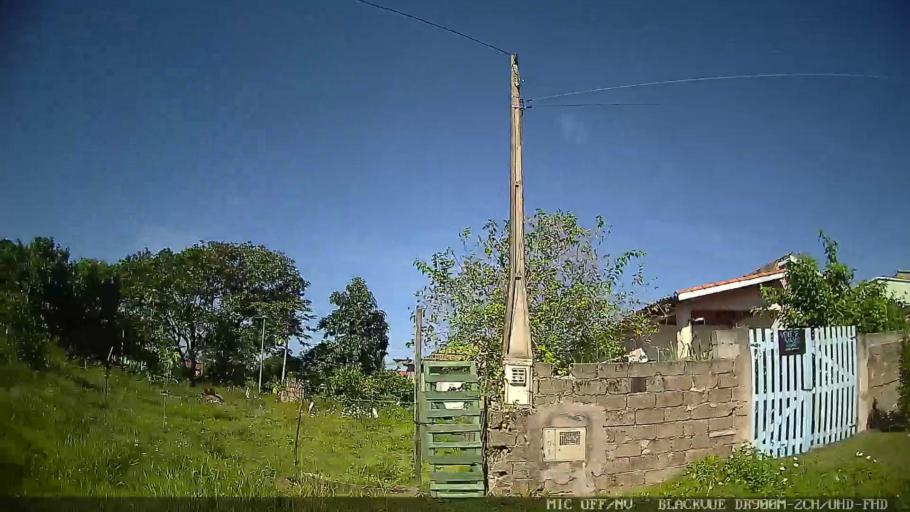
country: BR
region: Sao Paulo
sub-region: Peruibe
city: Peruibe
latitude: -24.2772
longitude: -46.9457
